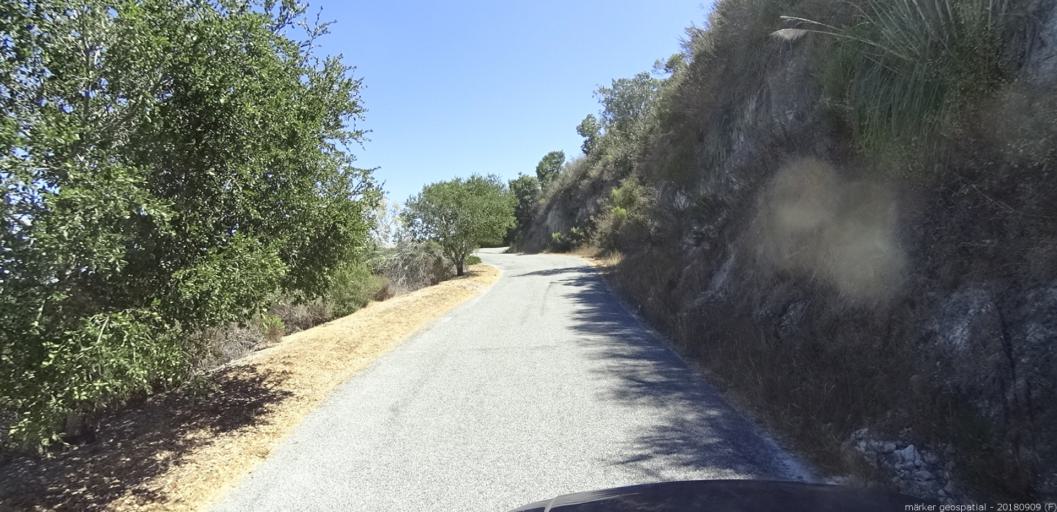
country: US
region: California
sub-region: Monterey County
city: Carmel Valley Village
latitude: 36.5544
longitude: -121.7499
